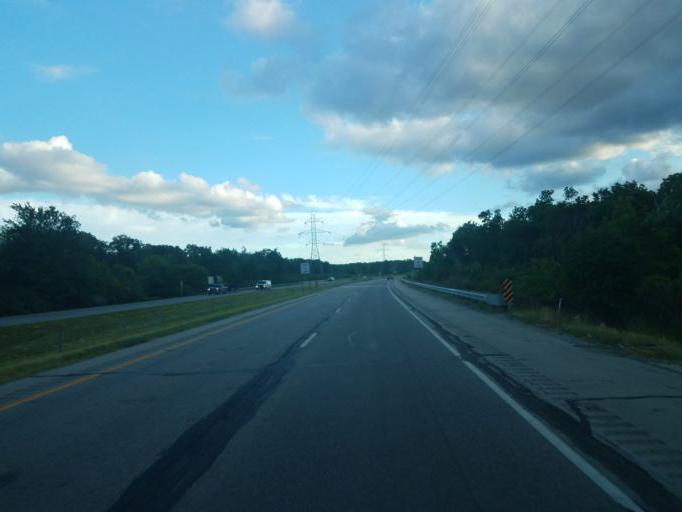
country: US
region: Indiana
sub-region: Allen County
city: Huntertown
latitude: 41.2386
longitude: -85.0931
